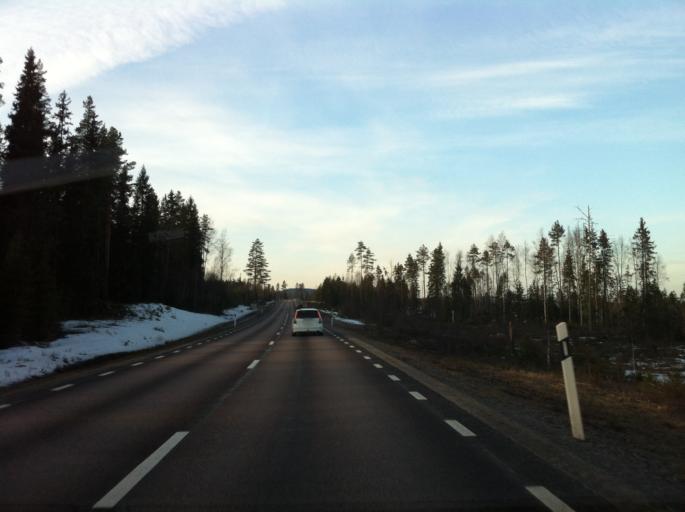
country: SE
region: Vaermland
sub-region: Filipstads Kommun
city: Lesjofors
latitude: 60.0570
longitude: 14.1411
